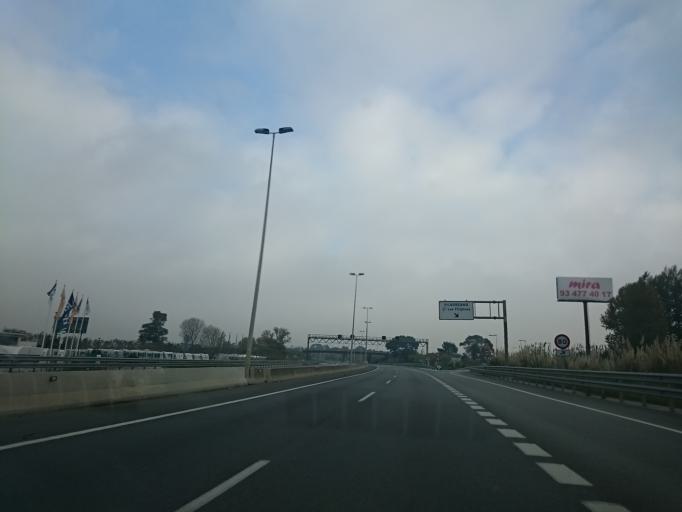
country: ES
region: Catalonia
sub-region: Provincia de Barcelona
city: Viladecans
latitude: 41.2769
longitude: 2.0498
